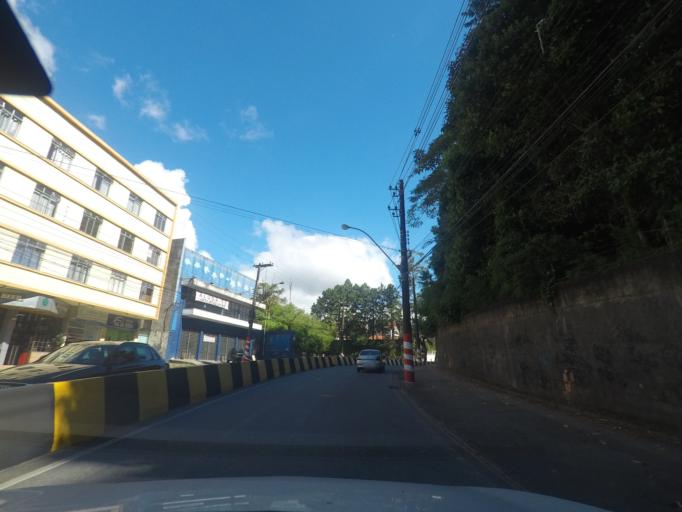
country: BR
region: Rio de Janeiro
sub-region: Teresopolis
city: Teresopolis
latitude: -22.4280
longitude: -42.9807
